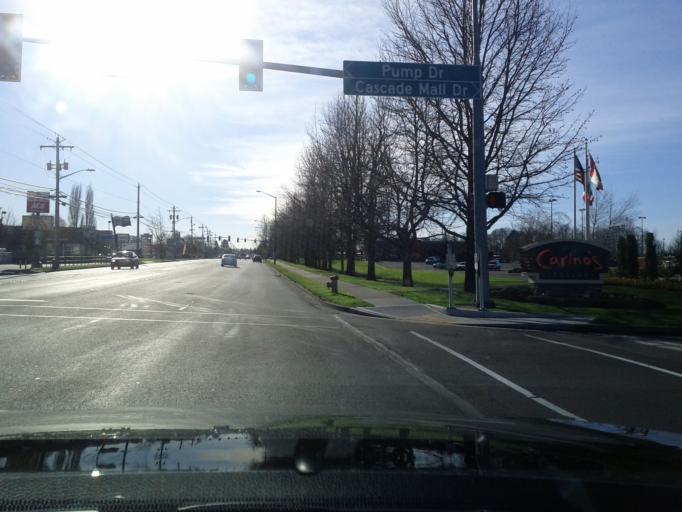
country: US
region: Washington
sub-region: Skagit County
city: Burlington
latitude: 48.4619
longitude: -122.3359
